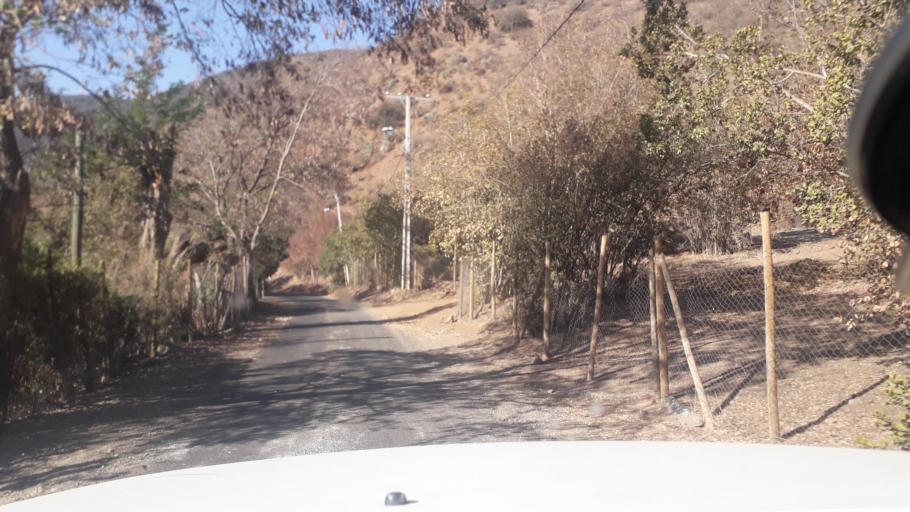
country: CL
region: Valparaiso
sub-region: Provincia de Marga Marga
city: Limache
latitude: -33.0707
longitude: -71.0988
